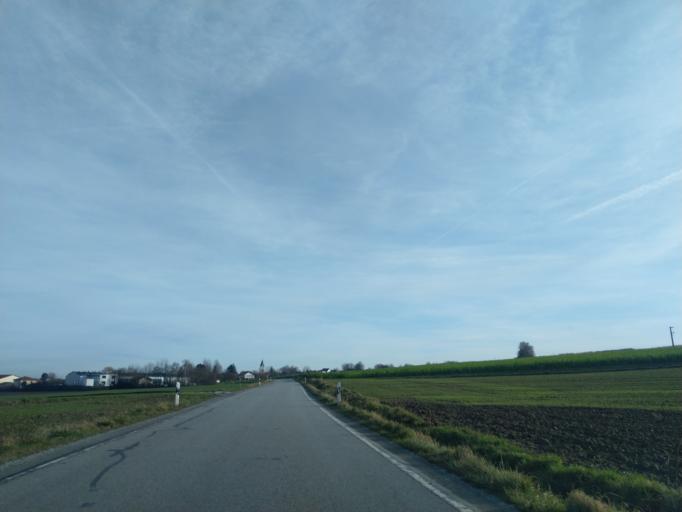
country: DE
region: Bavaria
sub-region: Lower Bavaria
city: Wallerfing
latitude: 48.6874
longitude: 12.8713
